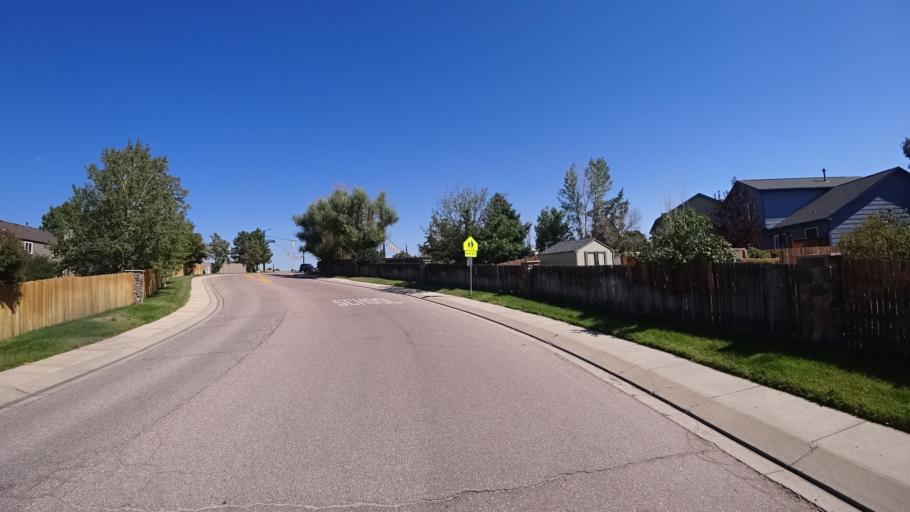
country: US
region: Colorado
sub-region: El Paso County
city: Black Forest
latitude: 38.9536
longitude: -104.7324
